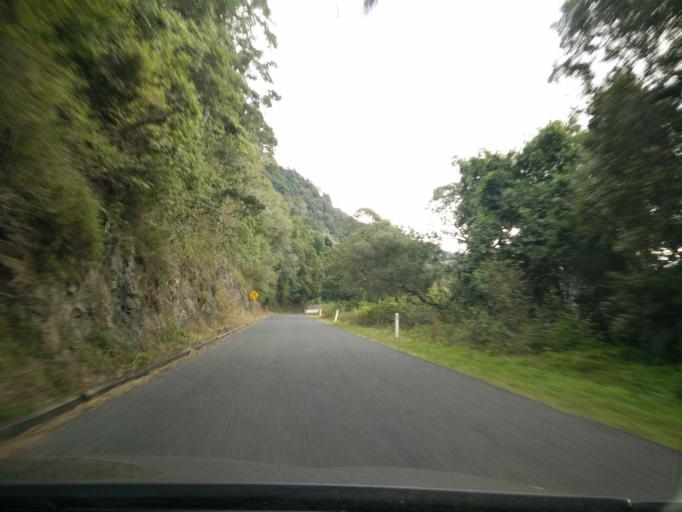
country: AU
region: New South Wales
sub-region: Kiama
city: Jamberoo
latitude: -34.6969
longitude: 150.7968
